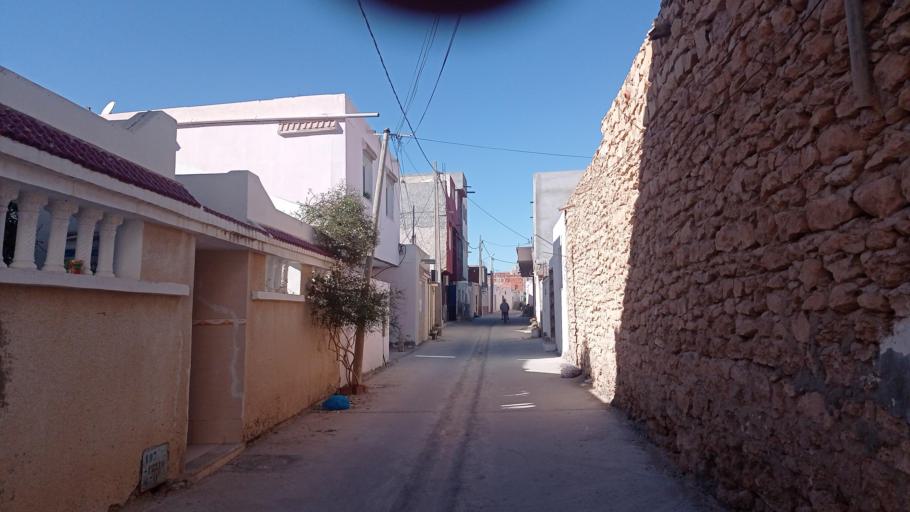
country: TN
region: Qabis
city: Gabes
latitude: 33.8422
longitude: 10.1171
